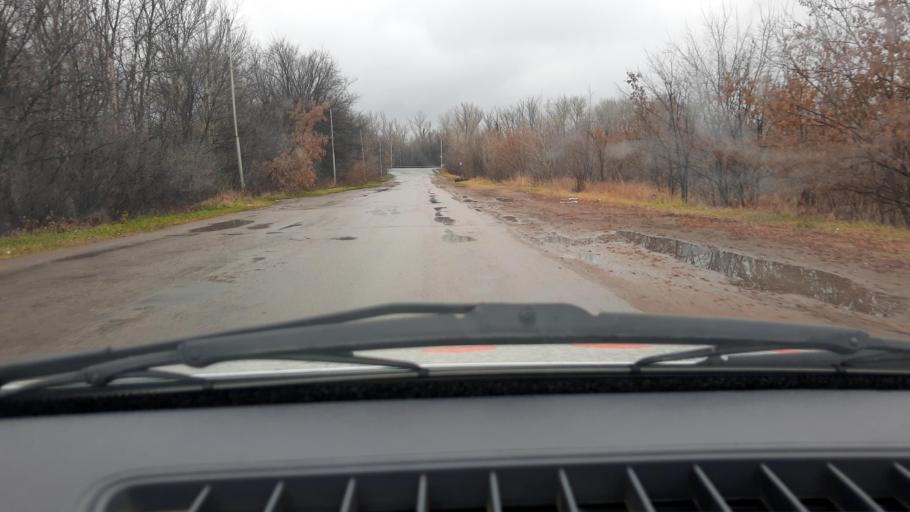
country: RU
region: Bashkortostan
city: Iglino
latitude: 54.7968
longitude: 56.2105
